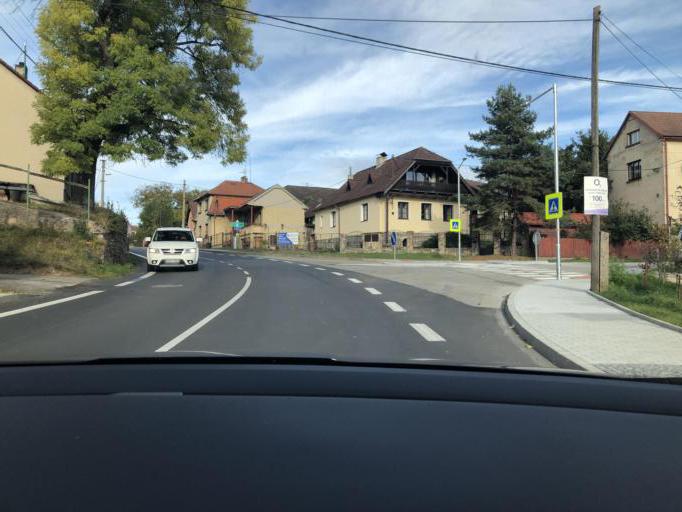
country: CZ
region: Central Bohemia
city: Divisov
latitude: 49.7898
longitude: 14.8787
